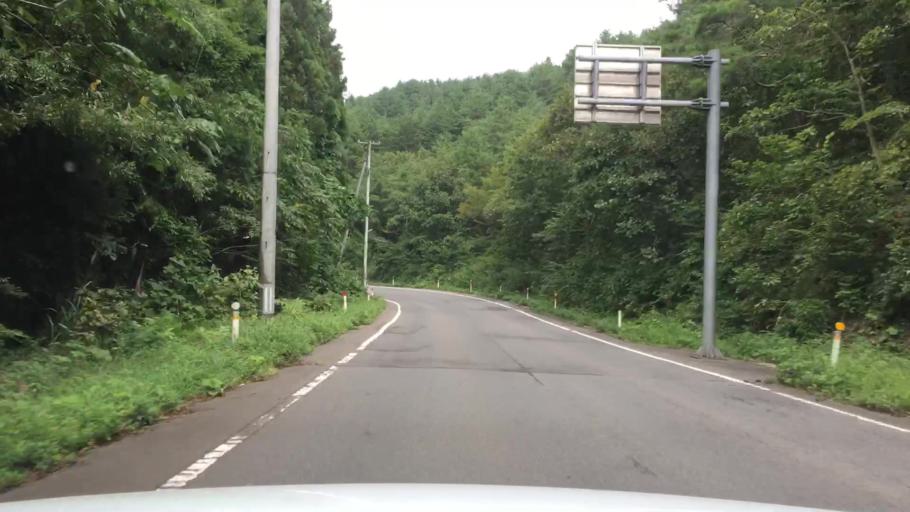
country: JP
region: Aomori
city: Shimokizukuri
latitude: 40.7213
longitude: 140.2584
